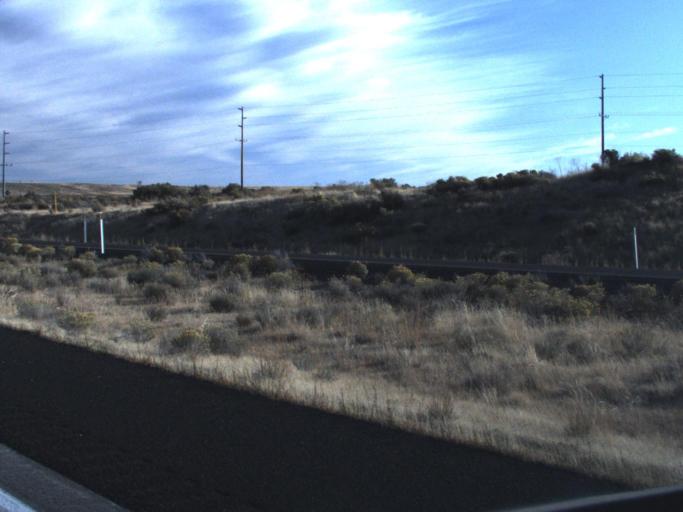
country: US
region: Washington
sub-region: Franklin County
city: Connell
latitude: 46.6556
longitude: -118.8526
